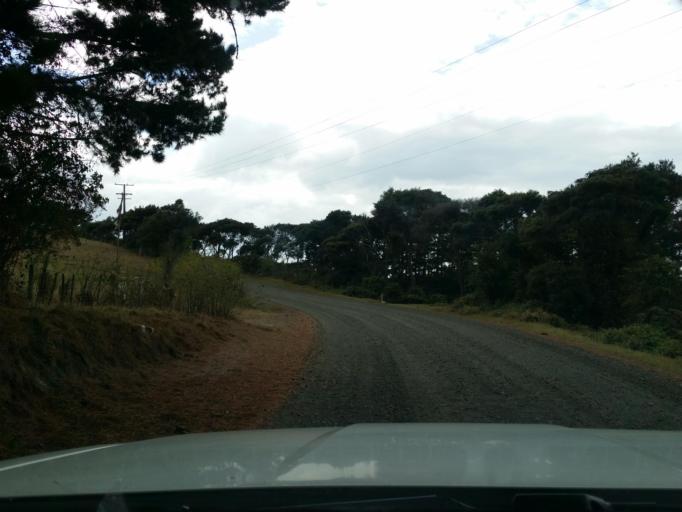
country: NZ
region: Auckland
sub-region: Auckland
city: Wellsford
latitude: -36.3184
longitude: 174.1346
